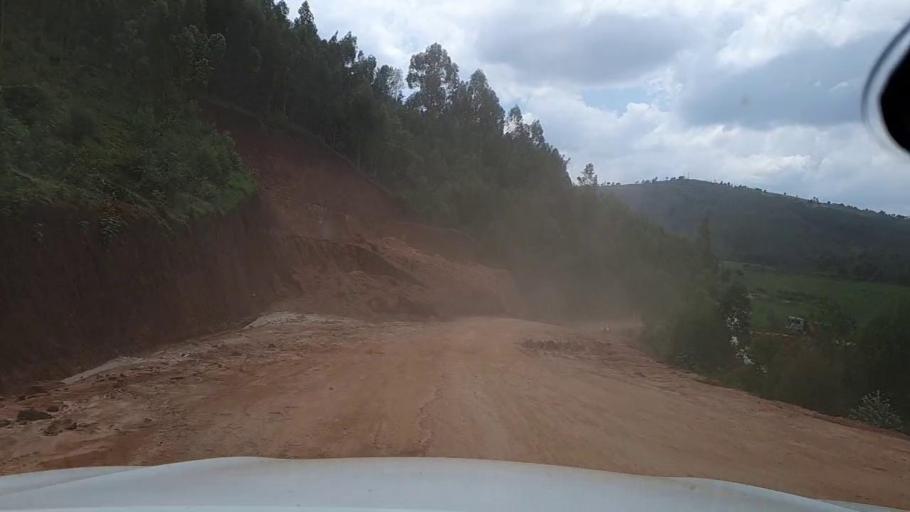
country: RW
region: Southern Province
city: Butare
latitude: -2.6964
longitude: 29.5553
